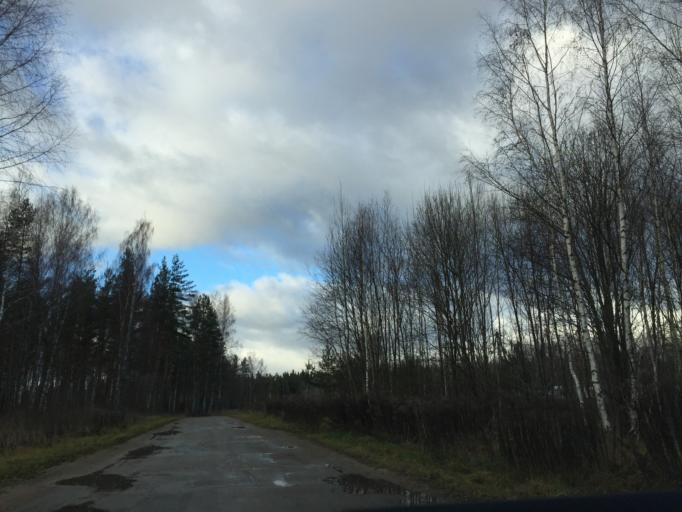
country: LV
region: Koceni
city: Koceni
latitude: 57.5372
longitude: 25.3792
